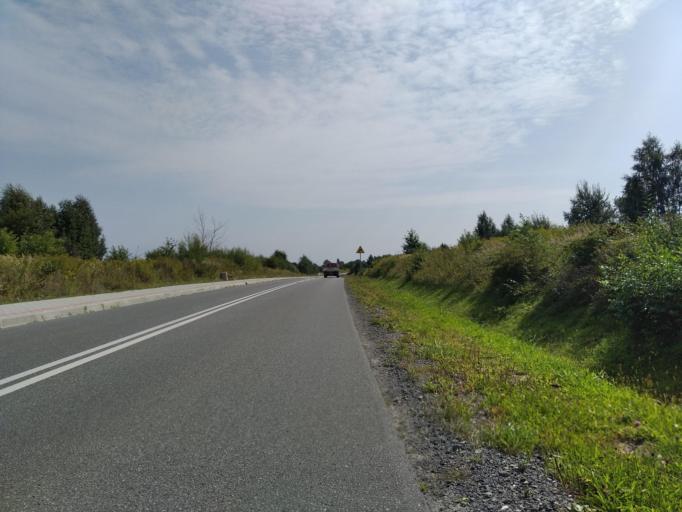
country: PL
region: Subcarpathian Voivodeship
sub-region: Powiat ropczycko-sedziszowski
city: Ropczyce
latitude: 50.0695
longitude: 21.5967
